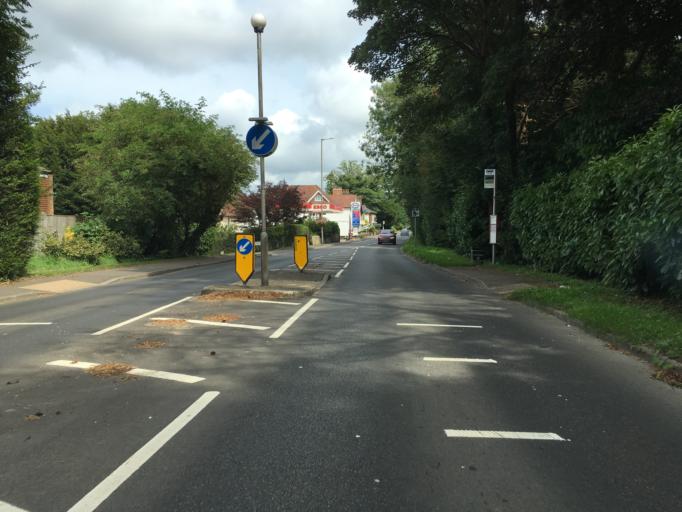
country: GB
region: England
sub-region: Kent
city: Royal Tunbridge Wells
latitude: 51.1310
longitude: 0.2066
